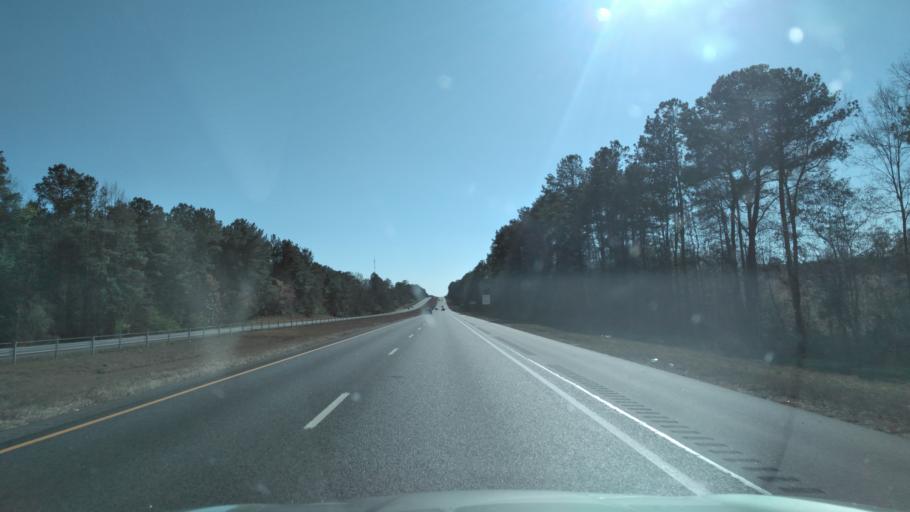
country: US
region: Alabama
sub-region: Butler County
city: Georgiana
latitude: 31.6444
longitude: -86.7820
